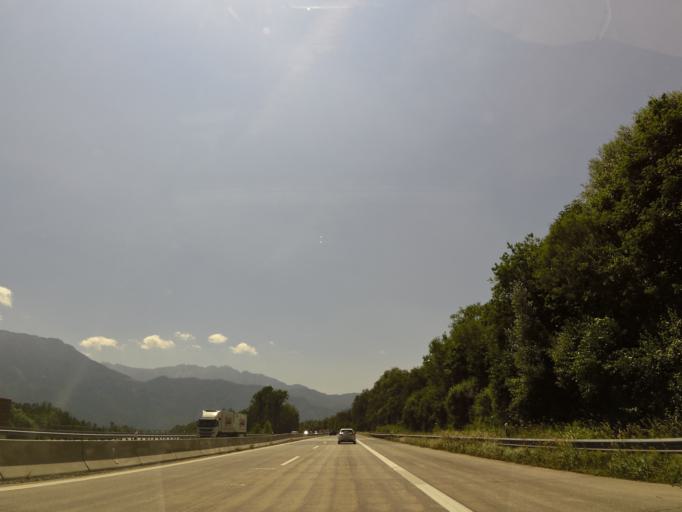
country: DE
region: Bavaria
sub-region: Upper Bavaria
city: Oberaudorf
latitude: 47.6619
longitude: 12.1832
